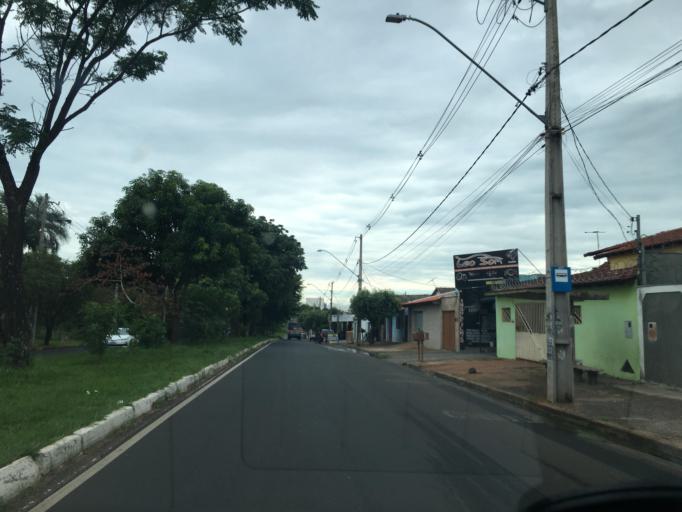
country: BR
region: Minas Gerais
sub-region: Uberlandia
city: Uberlandia
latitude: -18.9290
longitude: -48.3174
